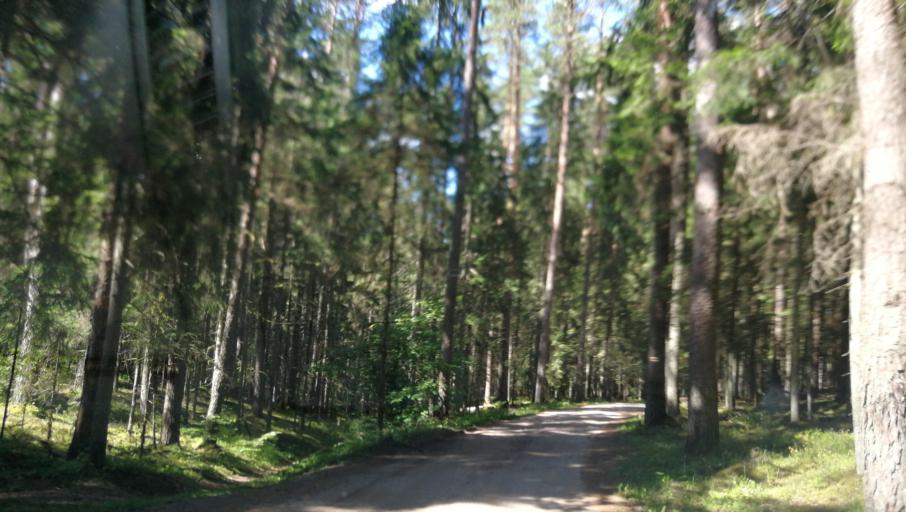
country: LV
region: Cesu Rajons
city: Cesis
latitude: 57.2859
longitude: 25.2130
